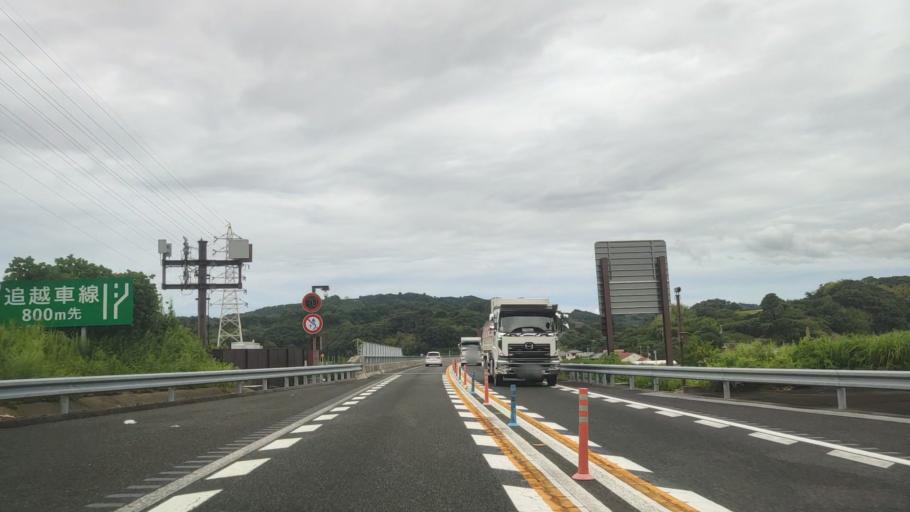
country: JP
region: Wakayama
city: Tanabe
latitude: 33.7521
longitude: 135.3587
